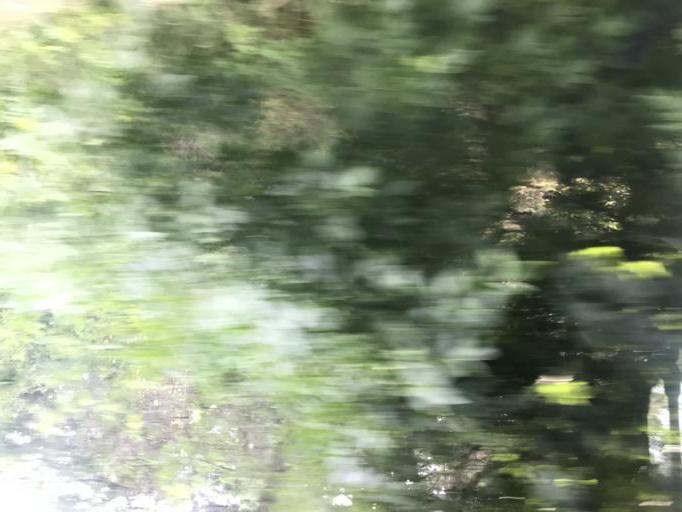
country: PL
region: Pomeranian Voivodeship
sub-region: Gdansk
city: Gdansk
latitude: 54.4014
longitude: 18.6295
